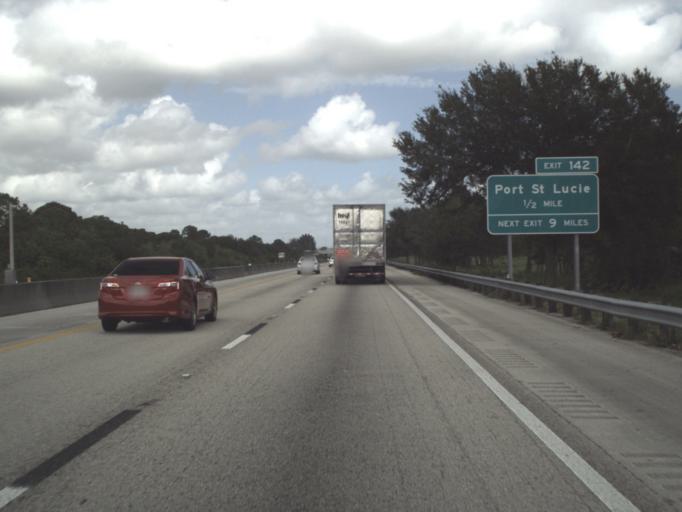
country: US
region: Florida
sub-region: Saint Lucie County
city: Port Saint Lucie
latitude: 27.2665
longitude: -80.3544
